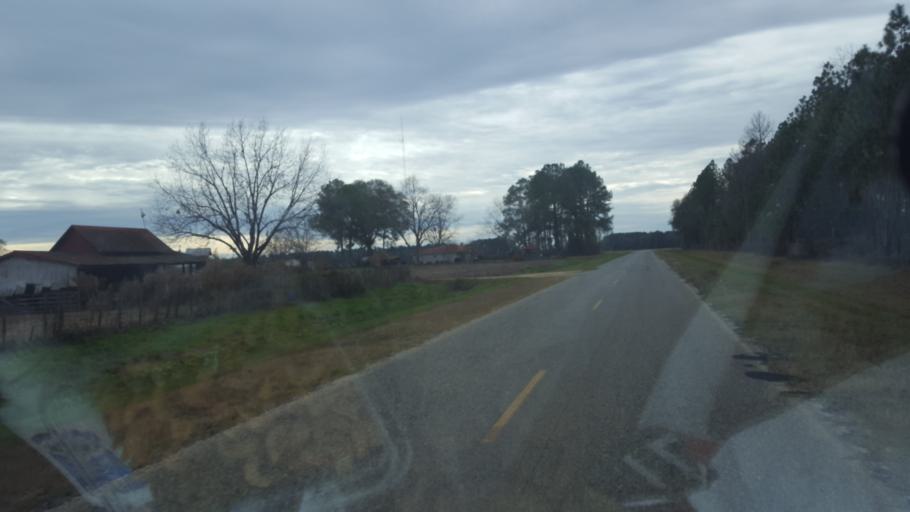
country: US
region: Georgia
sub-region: Berrien County
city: Enigma
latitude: 31.3403
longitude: -83.2722
